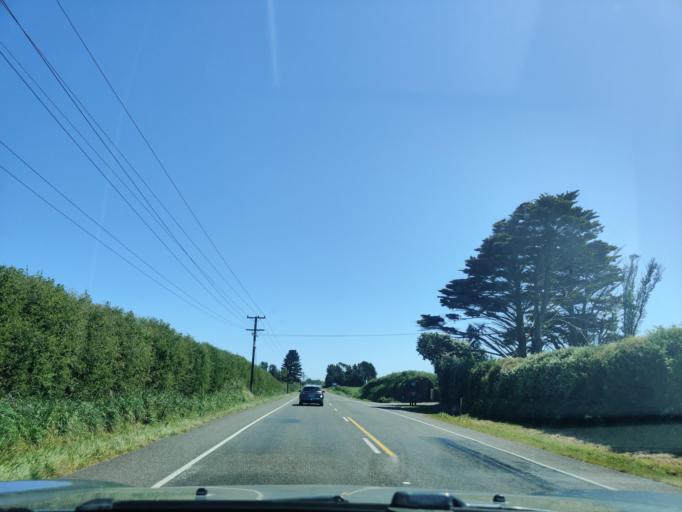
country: NZ
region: Taranaki
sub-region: South Taranaki District
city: Hawera
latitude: -39.6077
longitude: 174.3193
